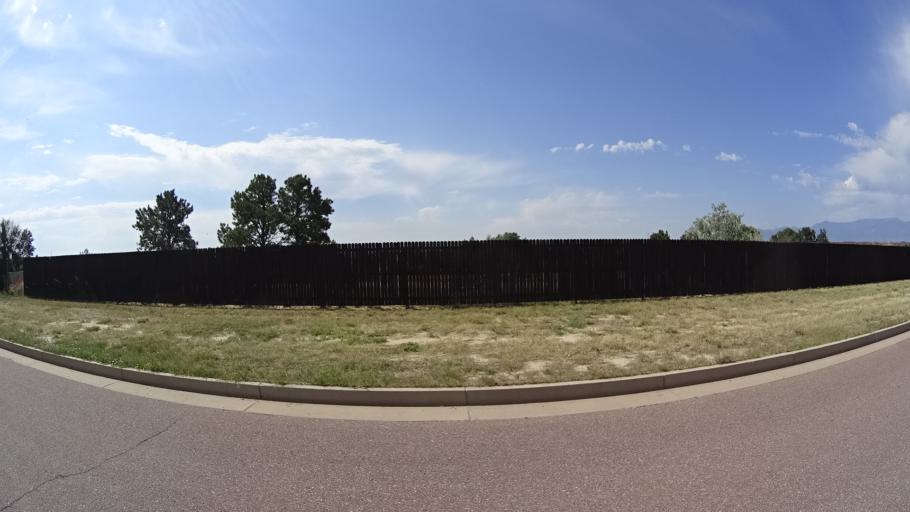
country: US
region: Colorado
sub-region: El Paso County
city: Cimarron Hills
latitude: 38.9265
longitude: -104.6787
